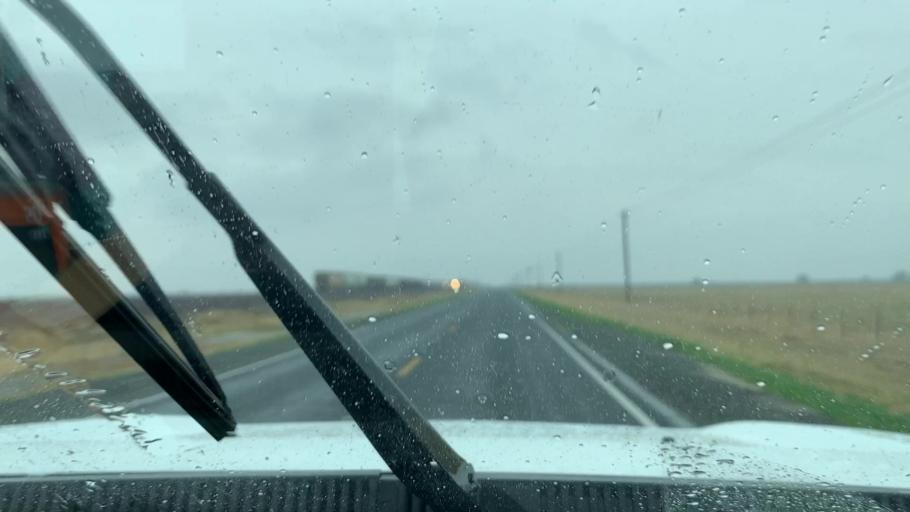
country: US
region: California
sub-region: Tulare County
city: Alpaugh
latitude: 35.9084
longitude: -119.4176
